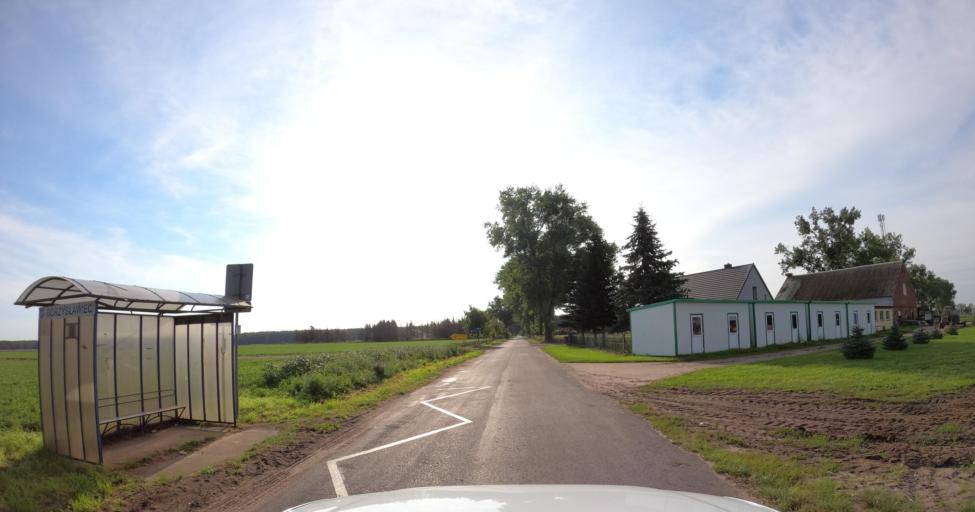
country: PL
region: West Pomeranian Voivodeship
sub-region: Powiat goleniowski
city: Goleniow
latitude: 53.5151
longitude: 14.7277
